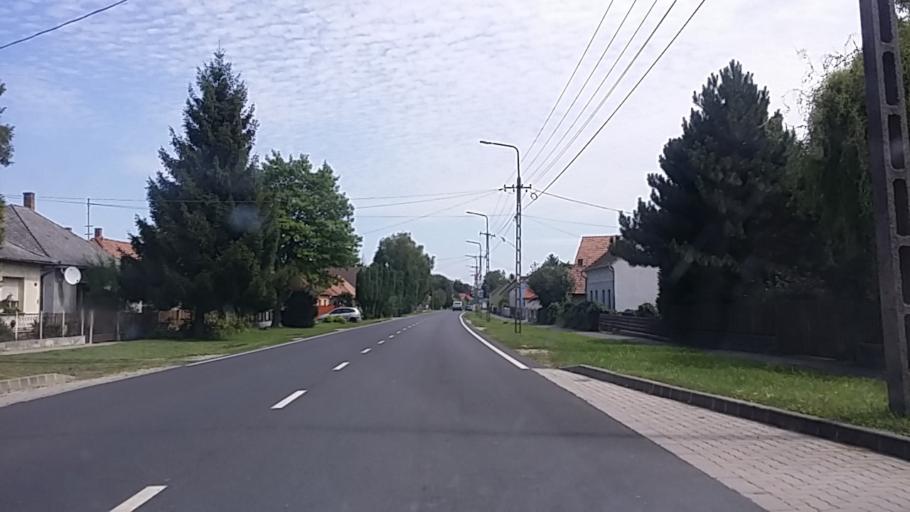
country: HU
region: Somogy
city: Taszar
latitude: 46.3634
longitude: 18.0025
